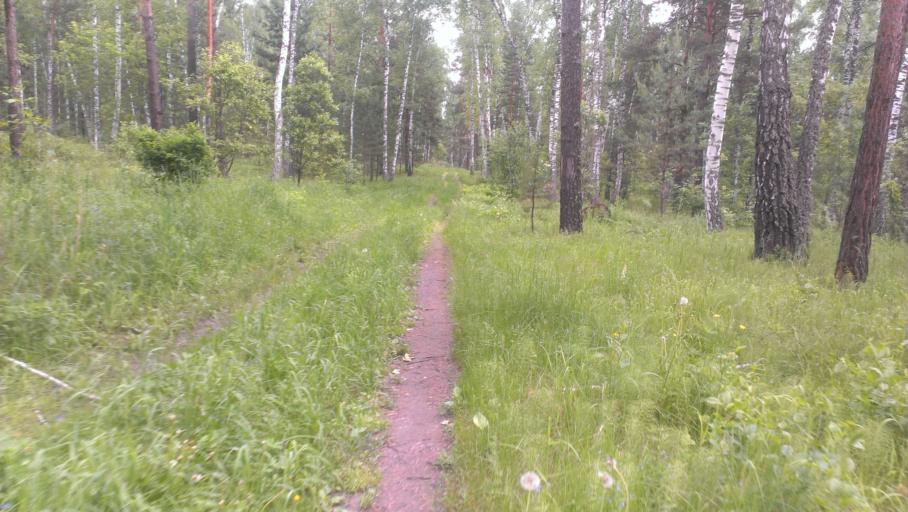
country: RU
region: Altai Krai
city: Sannikovo
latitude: 53.3463
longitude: 84.0413
